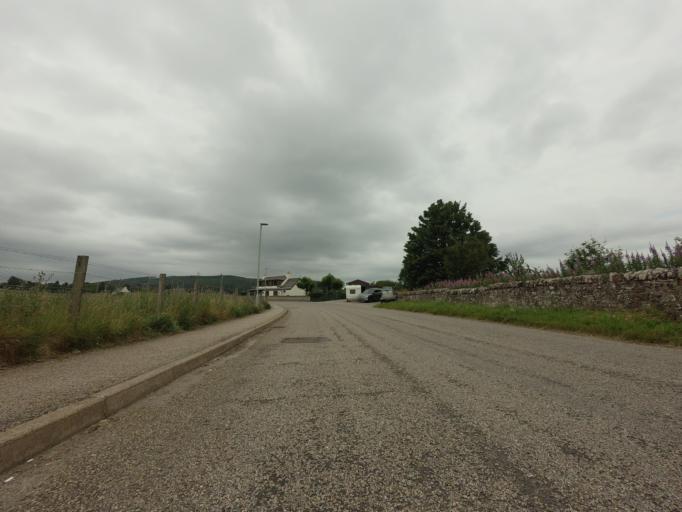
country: GB
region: Scotland
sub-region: Highland
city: Alness
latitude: 57.8847
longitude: -4.3664
